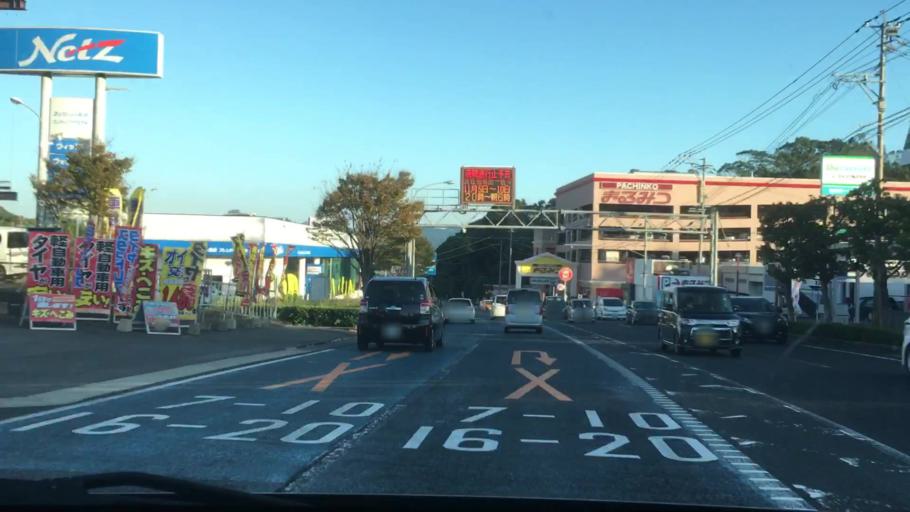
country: JP
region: Nagasaki
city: Sasebo
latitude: 33.1574
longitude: 129.7666
